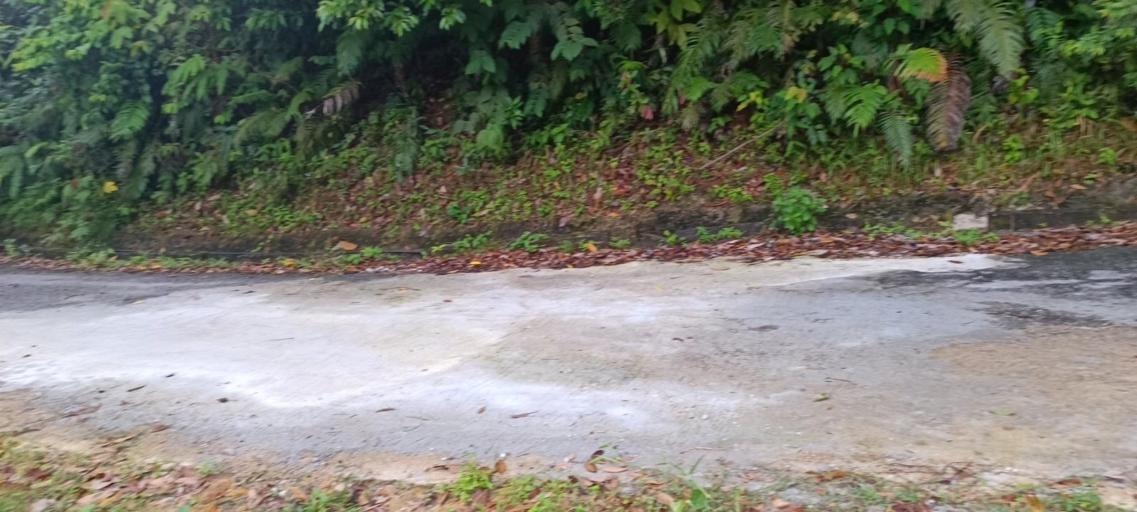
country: MY
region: Penang
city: Kampung Sungai Ara
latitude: 5.3877
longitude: 100.2596
